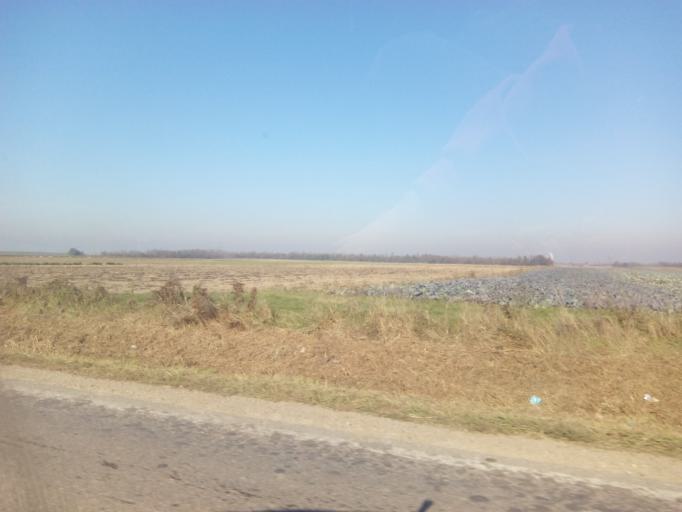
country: RS
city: Glozan
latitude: 45.2418
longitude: 19.6124
